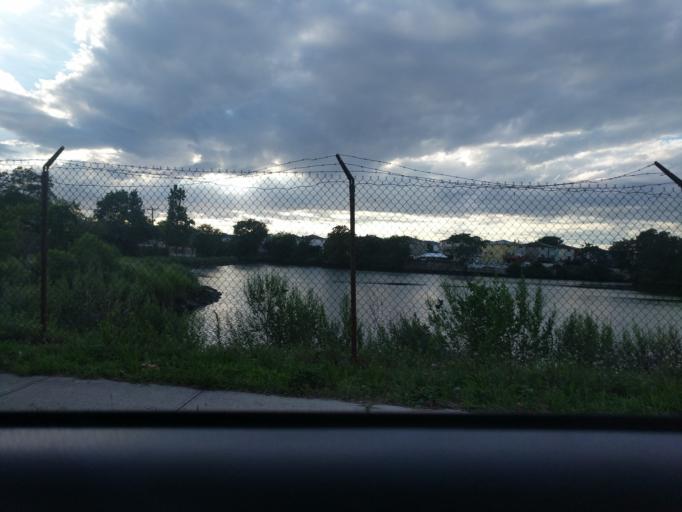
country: US
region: New York
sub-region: Nassau County
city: South Valley Stream
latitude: 40.6513
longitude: -73.7235
